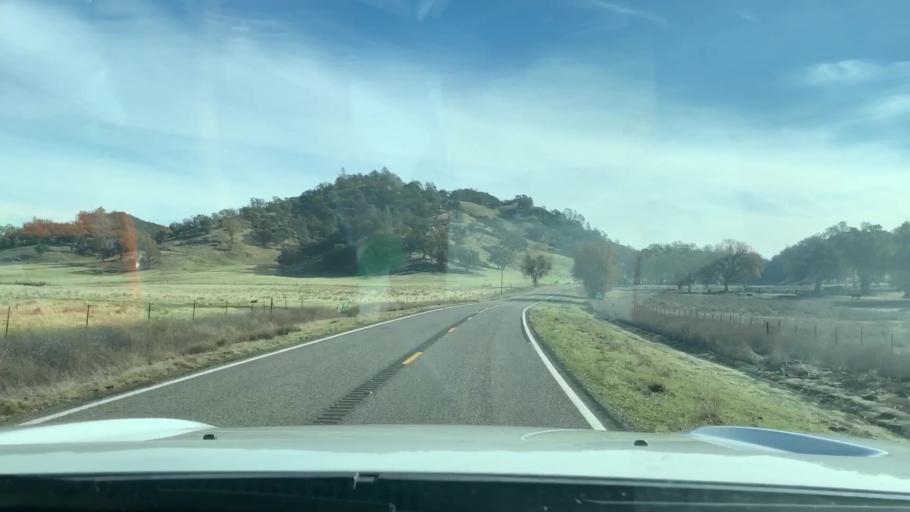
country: US
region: California
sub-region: Fresno County
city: Coalinga
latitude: 36.1738
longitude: -120.6749
